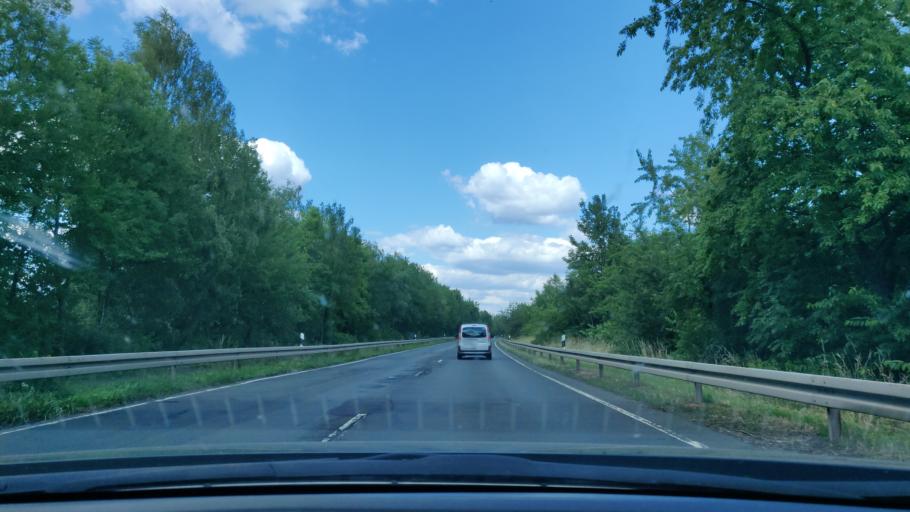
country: DE
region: Hesse
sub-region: Regierungsbezirk Kassel
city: Lohfelden
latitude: 51.2777
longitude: 9.5101
